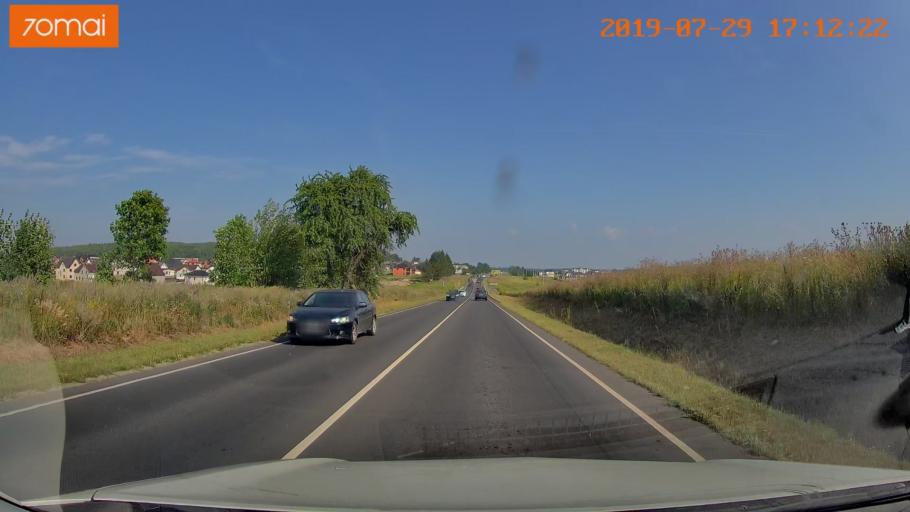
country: RU
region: Kaliningrad
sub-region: Gorod Kaliningrad
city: Kaliningrad
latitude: 54.7889
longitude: 20.3962
